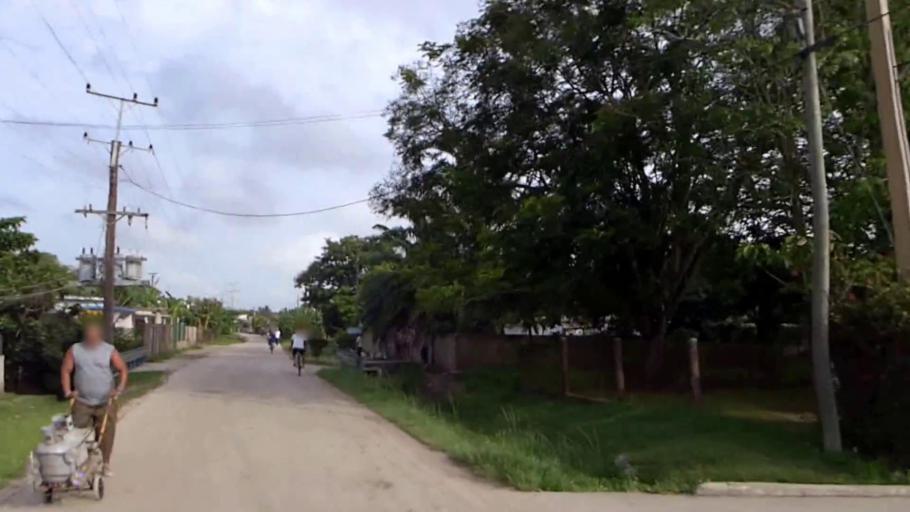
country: CU
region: Camaguey
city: Camaguey
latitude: 21.3810
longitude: -77.9396
